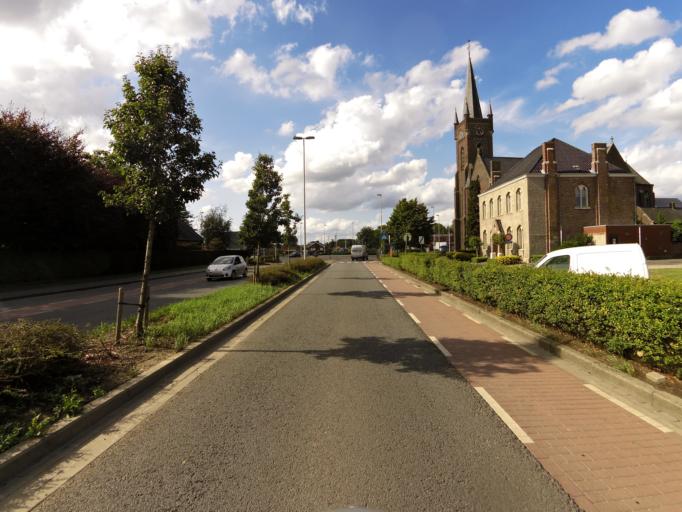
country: BE
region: Flanders
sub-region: Provincie West-Vlaanderen
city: Anzegem
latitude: 50.7977
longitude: 3.5013
